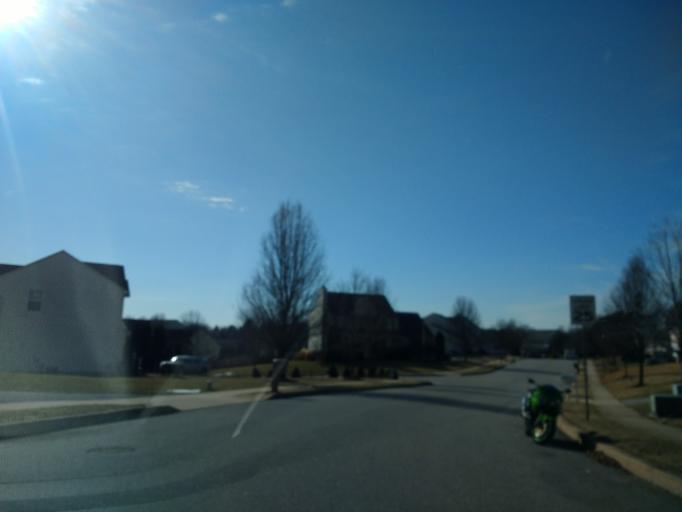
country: US
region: Pennsylvania
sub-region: York County
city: Dallastown
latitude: 39.9041
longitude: -76.6624
